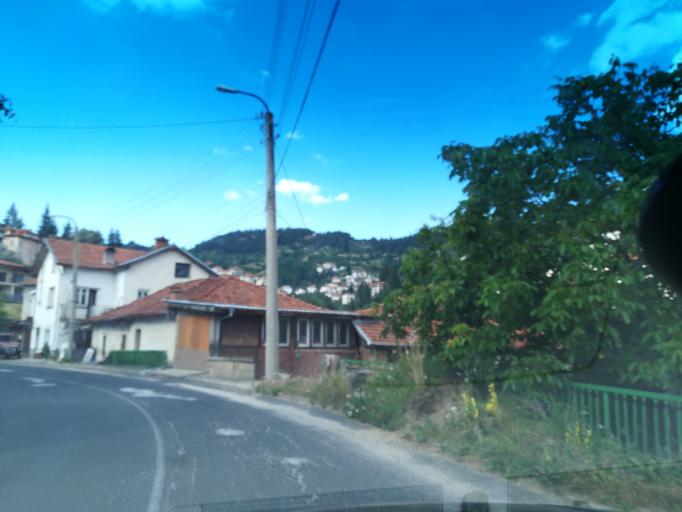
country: BG
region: Smolyan
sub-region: Obshtina Smolyan
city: Smolyan
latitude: 41.6563
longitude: 24.7745
